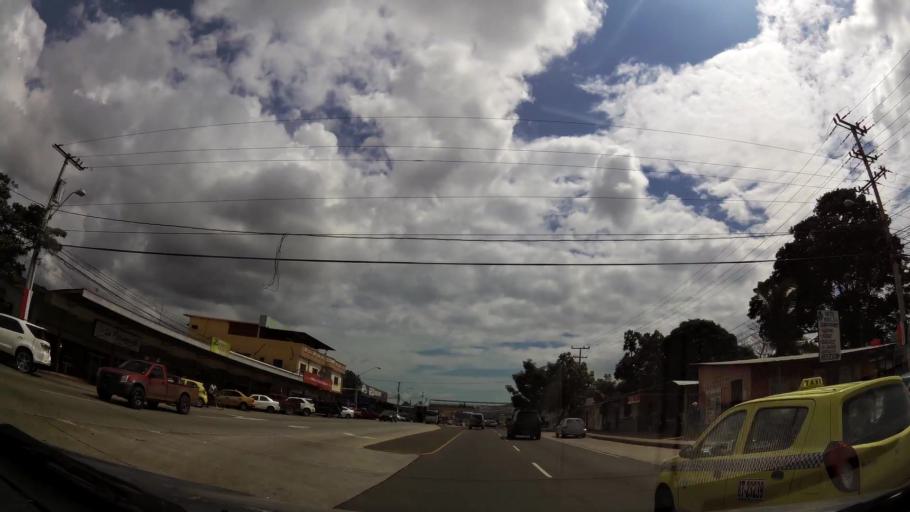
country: PA
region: Panama
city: Nuevo Arraijan
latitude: 8.9263
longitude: -79.7192
